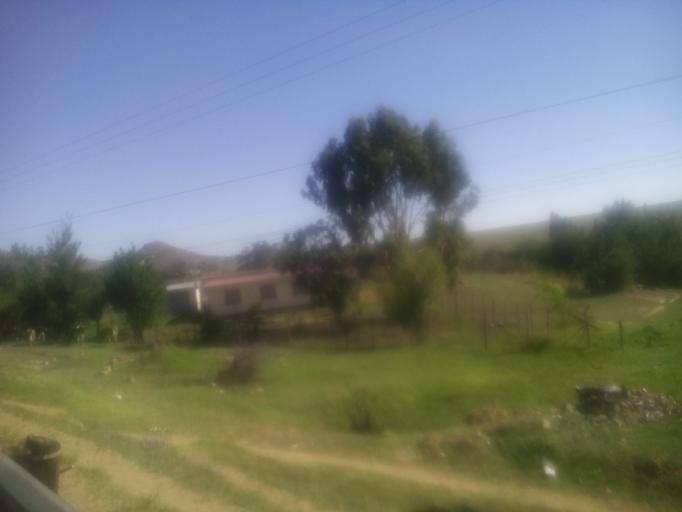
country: LS
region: Maseru
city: Maseru
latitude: -29.3083
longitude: 27.4651
